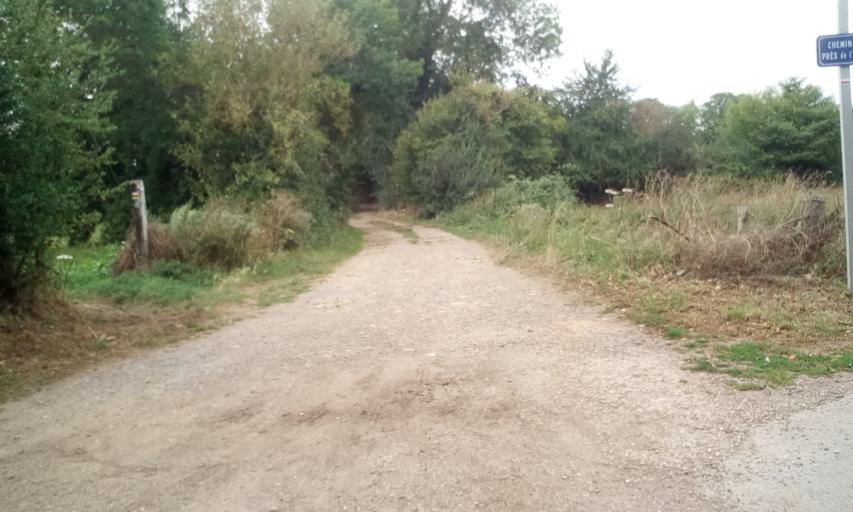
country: FR
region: Lower Normandy
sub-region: Departement du Calvados
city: Fontaine-Etoupefour
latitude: 49.1460
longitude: -0.4609
